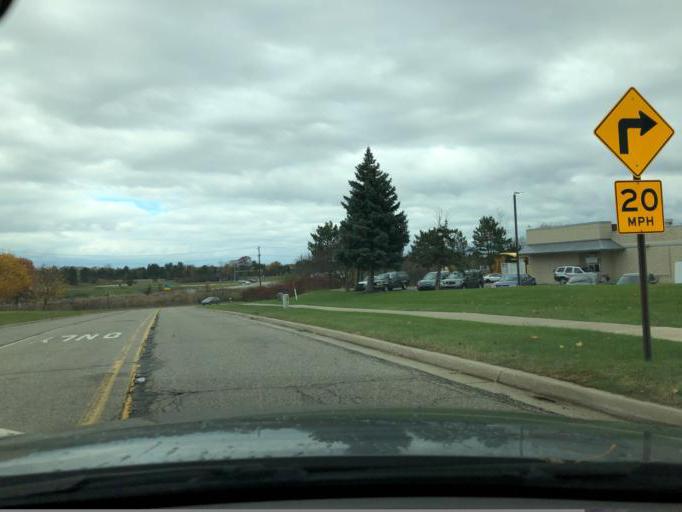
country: US
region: Michigan
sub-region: Washtenaw County
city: Ann Arbor
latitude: 42.2418
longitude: -83.7663
